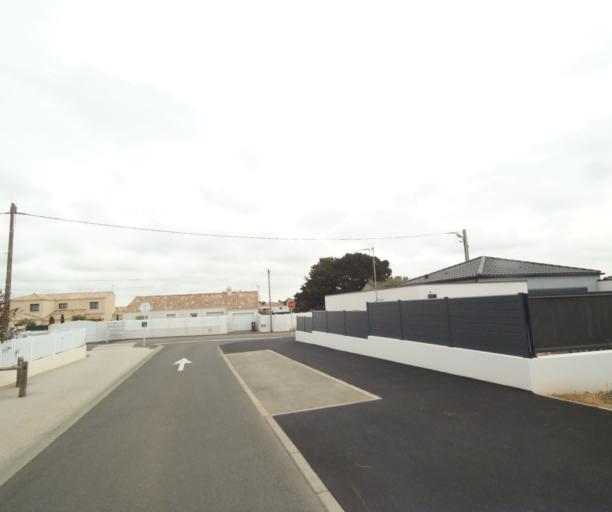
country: FR
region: Pays de la Loire
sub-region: Departement de la Vendee
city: Chateau-d'Olonne
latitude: 46.4767
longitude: -1.7409
